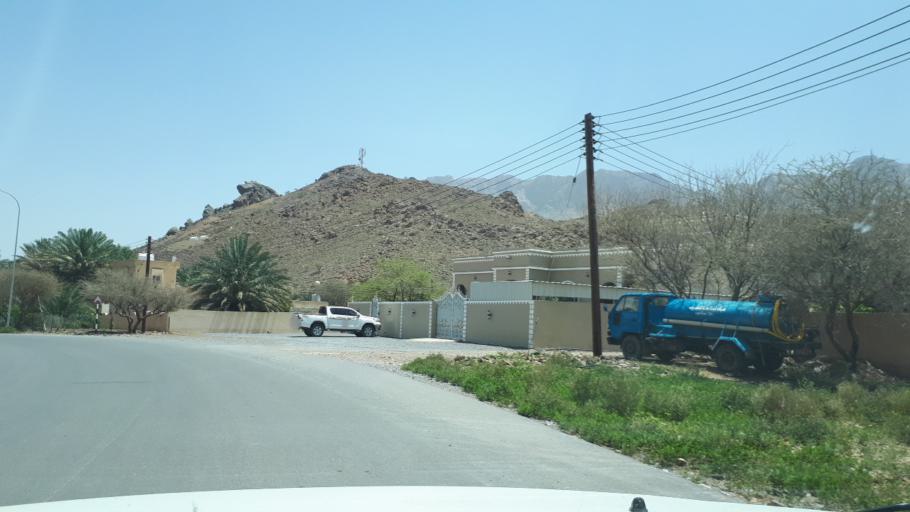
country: OM
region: Muhafazat ad Dakhiliyah
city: Bahla'
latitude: 23.1713
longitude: 57.1515
